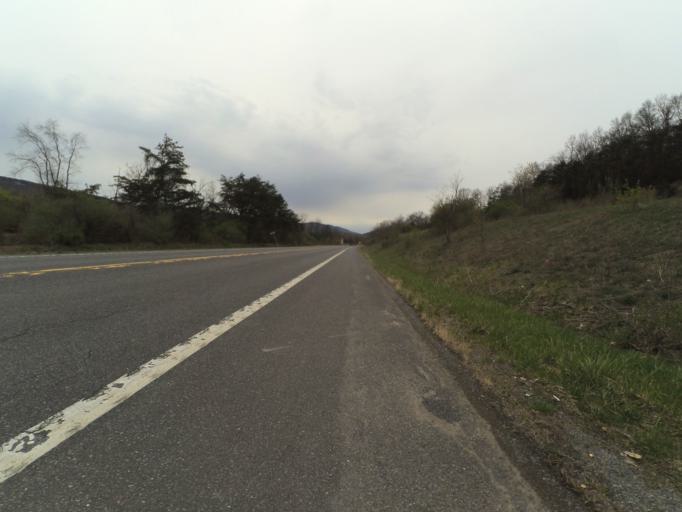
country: US
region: Pennsylvania
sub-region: Centre County
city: Milesburg
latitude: 40.9826
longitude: -77.7269
